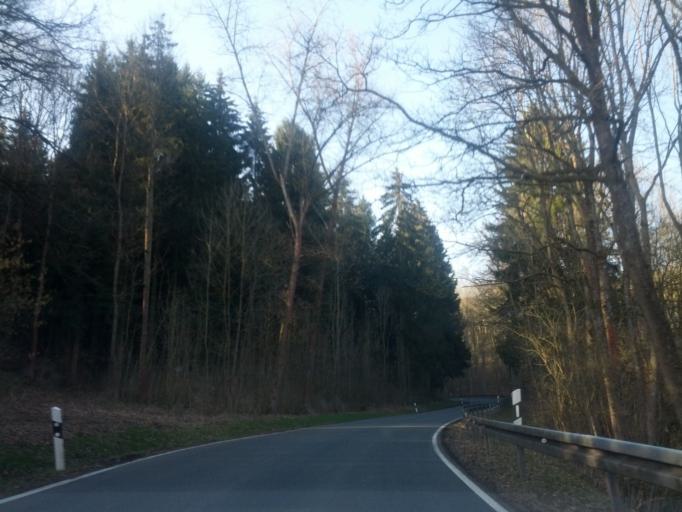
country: DE
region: Thuringia
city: Creuzburg
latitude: 51.0662
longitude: 10.2353
